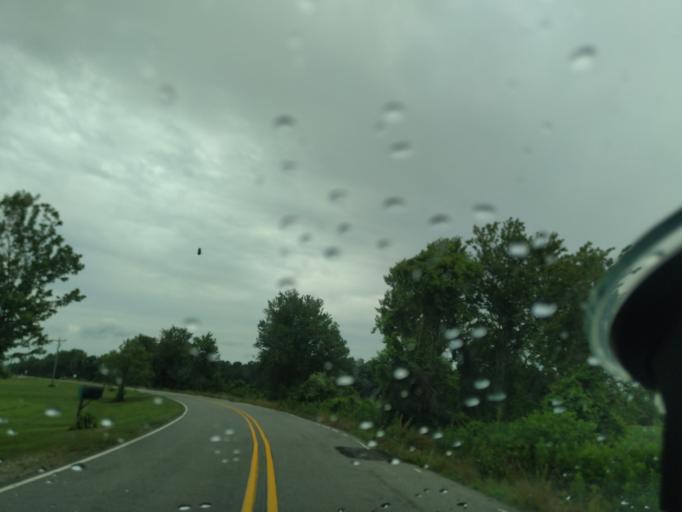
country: US
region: North Carolina
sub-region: Washington County
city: Plymouth
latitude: 35.7683
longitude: -76.5267
